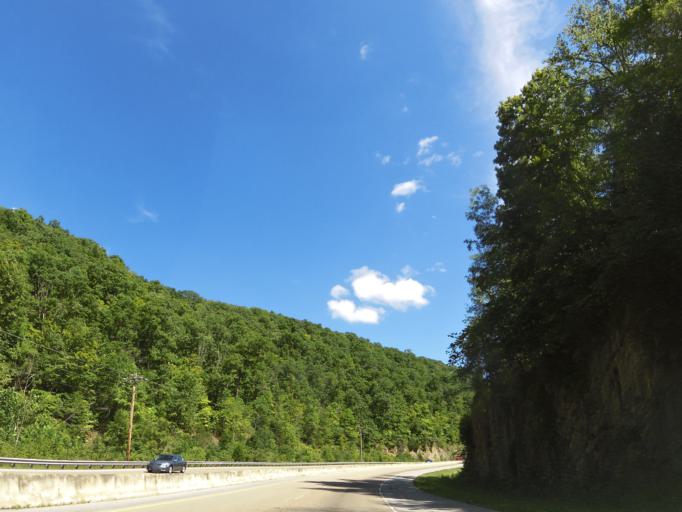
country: US
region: Tennessee
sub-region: Grainger County
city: Rutledge
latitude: 36.3669
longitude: -83.4355
